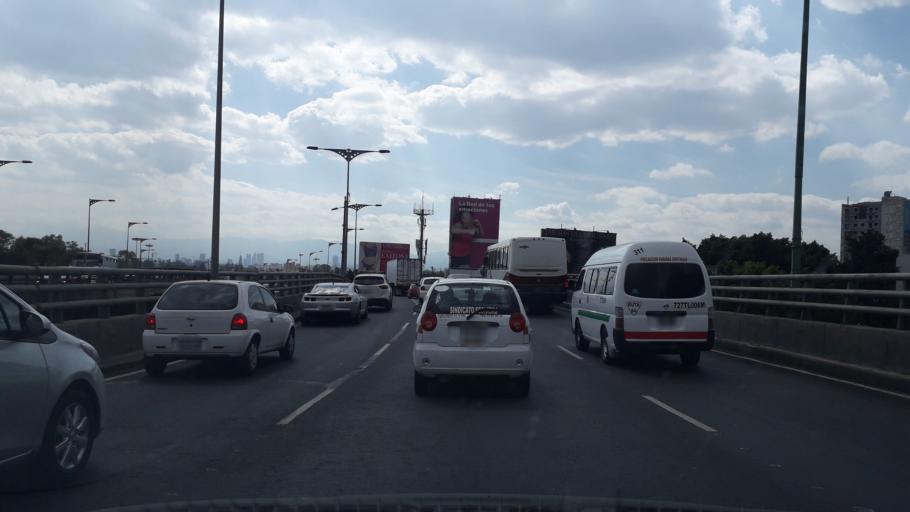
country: MX
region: Mexico
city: Colonia Lindavista
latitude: 19.5021
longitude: -99.1171
